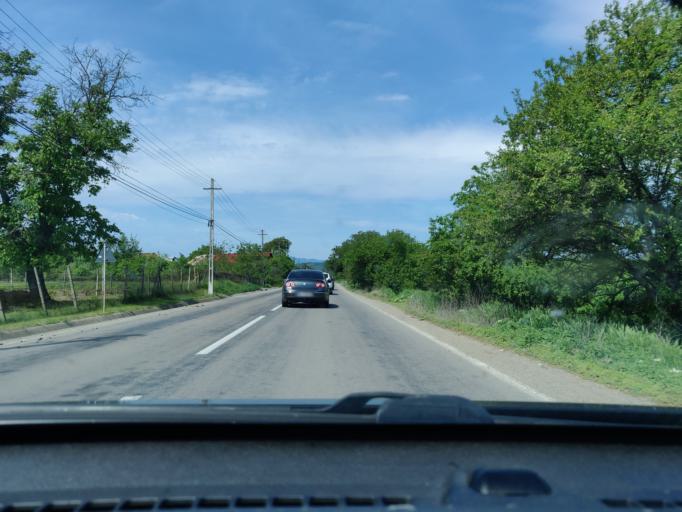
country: RO
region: Vrancea
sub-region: Comuna Vidra
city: Burca
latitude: 45.9127
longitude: 26.9427
